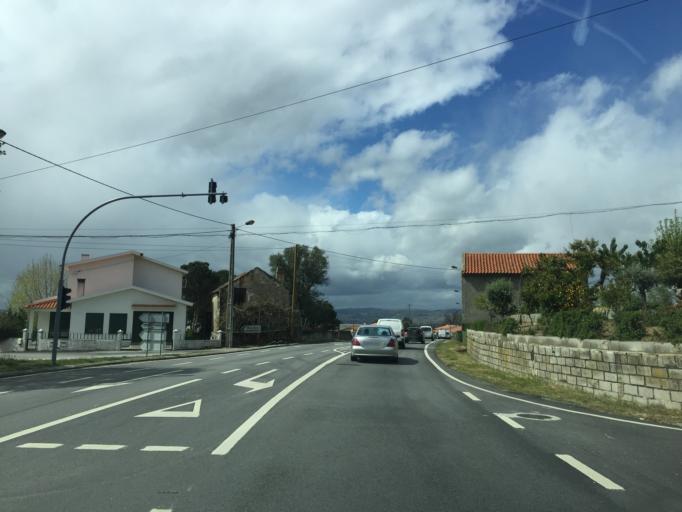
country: PT
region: Guarda
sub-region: Manteigas
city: Manteigas
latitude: 40.5040
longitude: -7.6145
